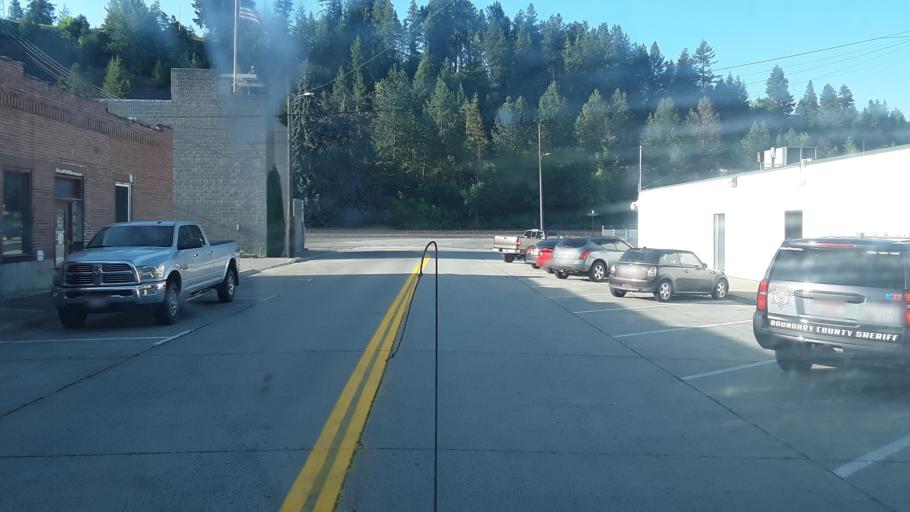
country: US
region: Idaho
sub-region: Boundary County
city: Bonners Ferry
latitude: 48.6962
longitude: -116.3131
